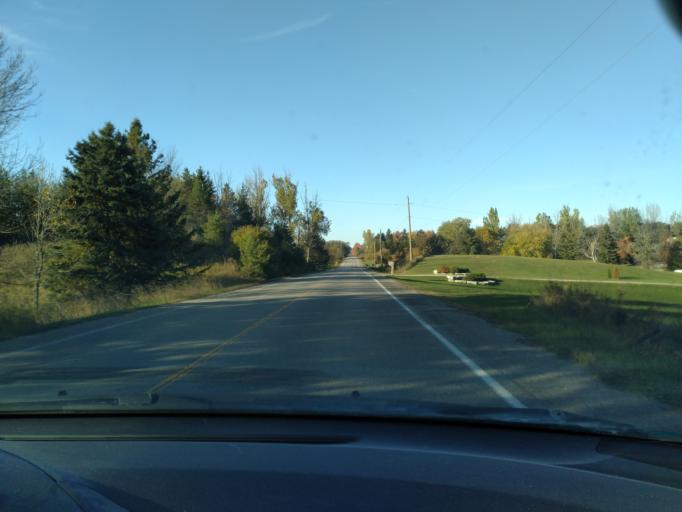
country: CA
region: Ontario
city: Bradford West Gwillimbury
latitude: 43.9484
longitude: -79.7148
